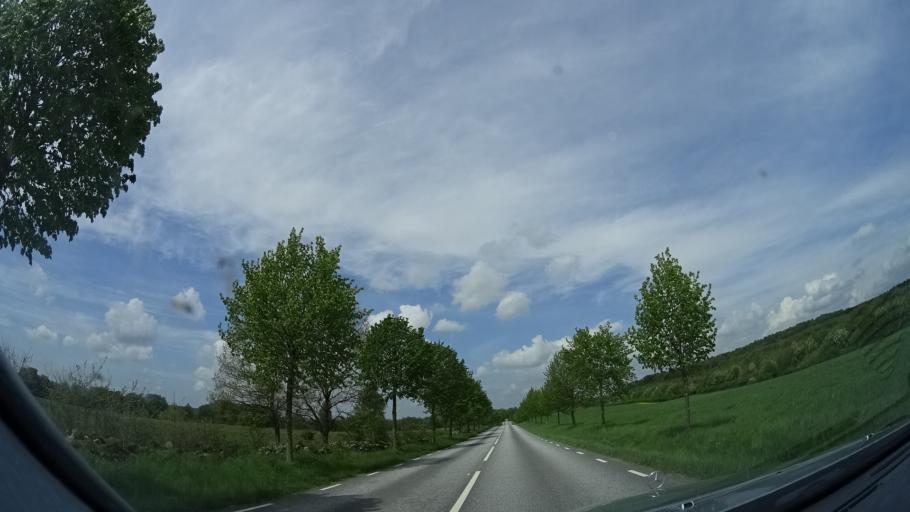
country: SE
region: Skane
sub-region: Sjobo Kommun
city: Sjoebo
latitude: 55.6688
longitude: 13.6677
